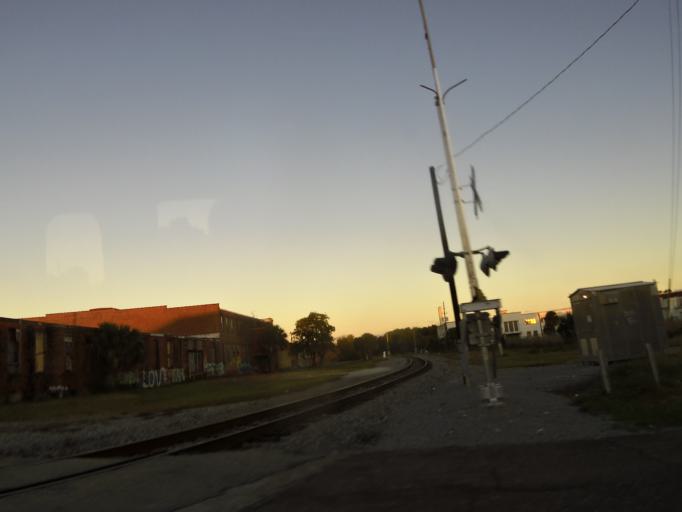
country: US
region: Florida
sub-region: Duval County
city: Jacksonville
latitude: 30.3511
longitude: -81.6506
